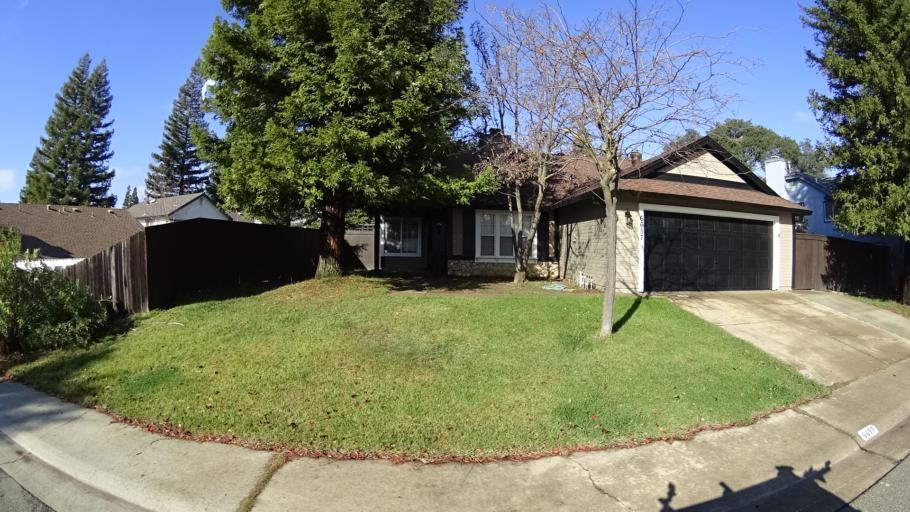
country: US
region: California
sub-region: Sacramento County
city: Antelope
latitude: 38.6874
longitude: -121.3281
